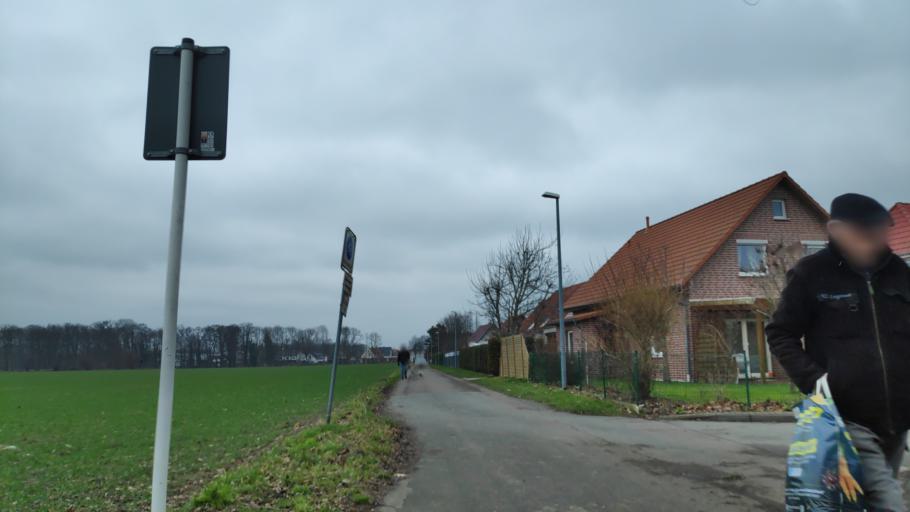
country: DE
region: North Rhine-Westphalia
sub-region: Regierungsbezirk Detmold
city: Minden
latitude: 52.3076
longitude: 8.8893
